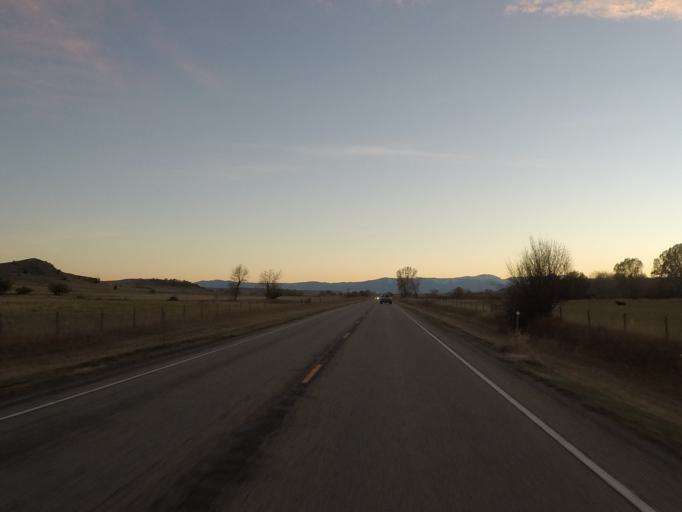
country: US
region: Montana
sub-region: Stillwater County
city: Columbus
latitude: 45.4481
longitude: -109.0807
